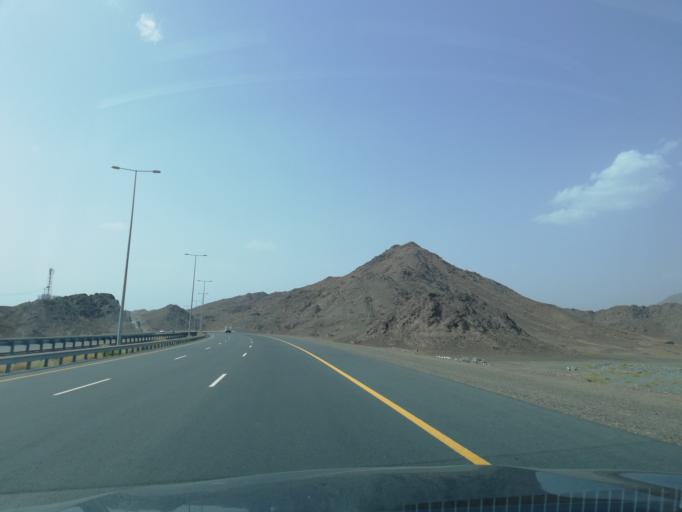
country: OM
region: Ash Sharqiyah
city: Ibra'
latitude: 22.9622
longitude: 58.2457
